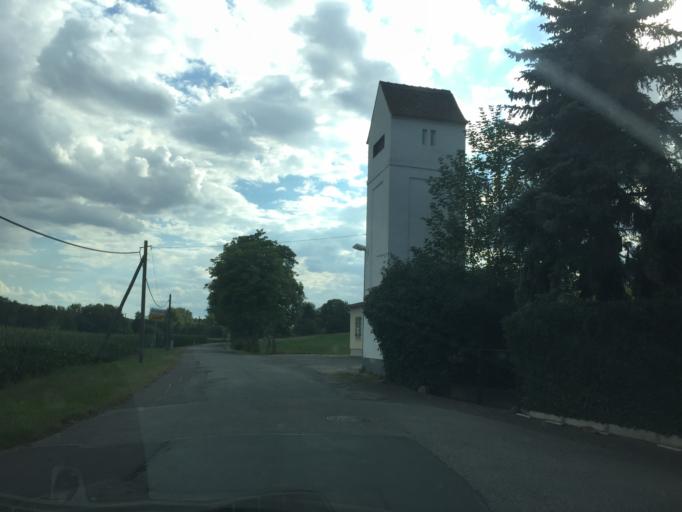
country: DE
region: Thuringia
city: Altenburg
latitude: 50.9643
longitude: 12.4562
